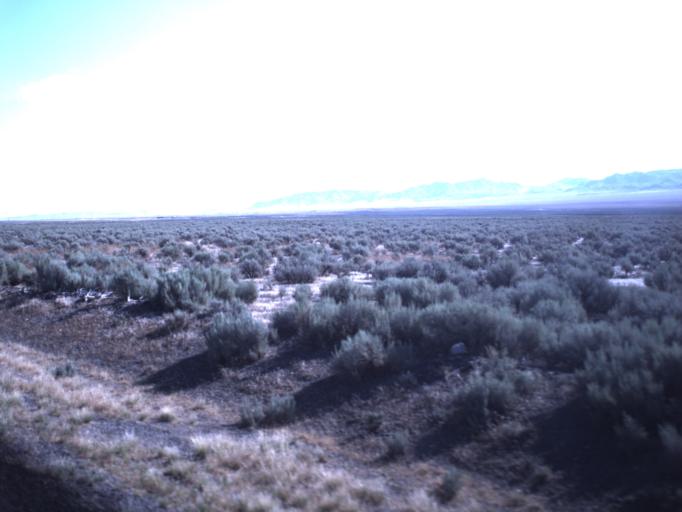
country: US
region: Utah
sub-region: Beaver County
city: Milford
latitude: 38.4254
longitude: -113.0098
